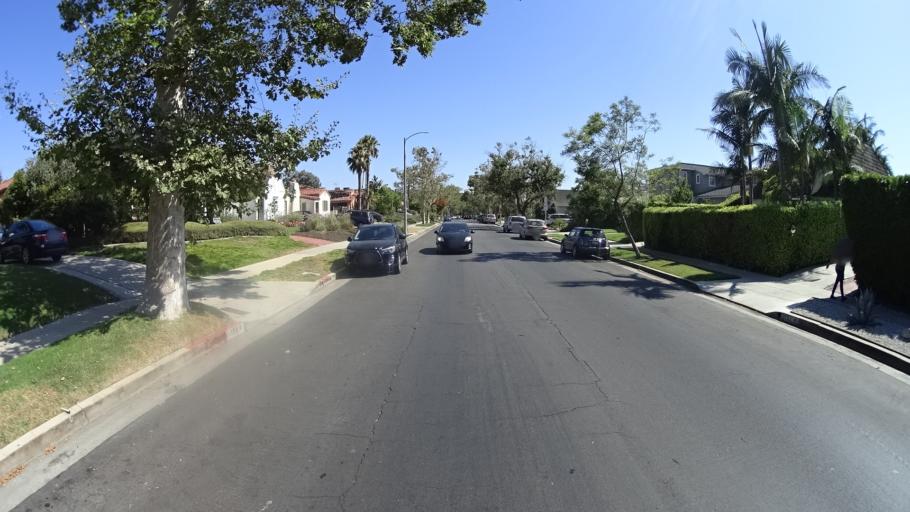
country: US
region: California
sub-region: Los Angeles County
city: West Hollywood
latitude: 34.0753
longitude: -118.3508
